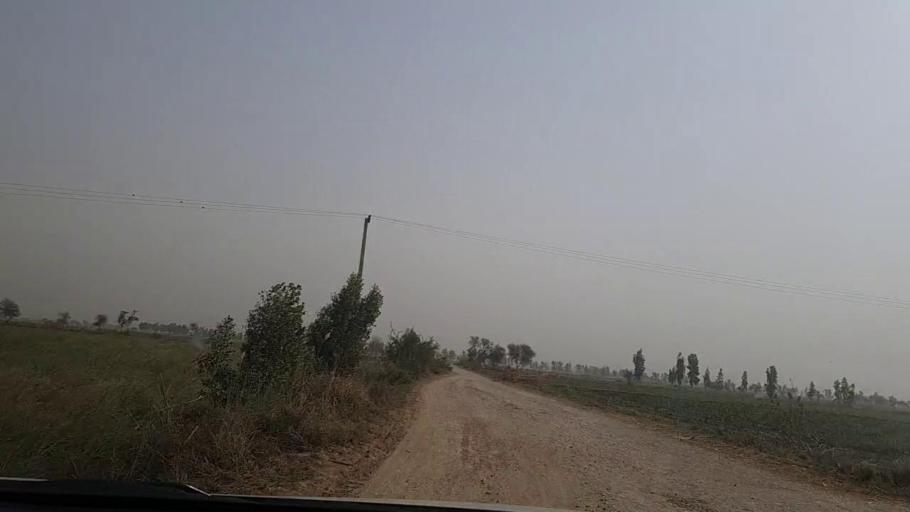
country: PK
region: Sindh
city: Pithoro
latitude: 25.4710
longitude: 69.2290
